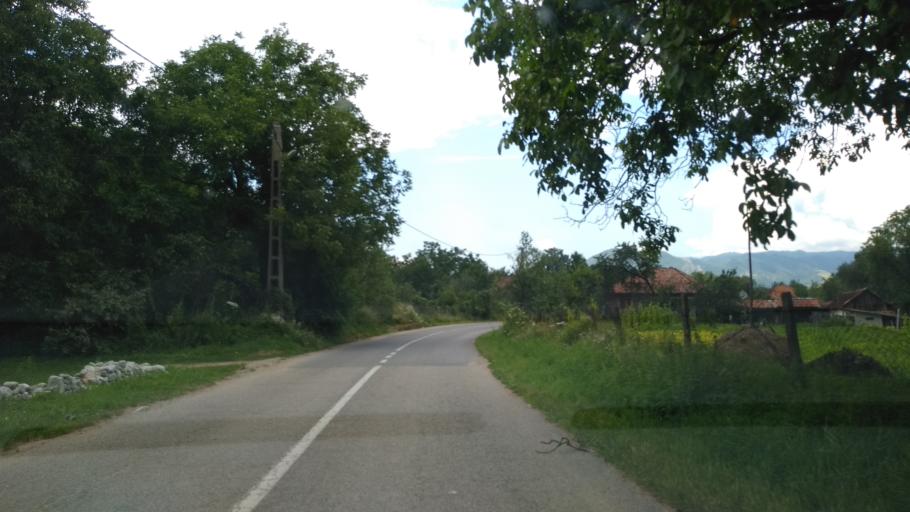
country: RO
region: Hunedoara
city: Salasu de Sus
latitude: 45.5053
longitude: 22.9508
